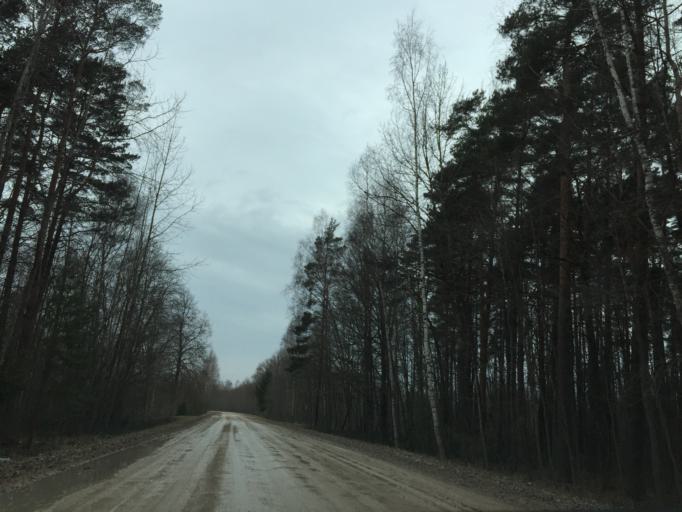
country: LV
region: Ozolnieku
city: Ozolnieki
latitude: 56.7005
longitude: 23.7353
